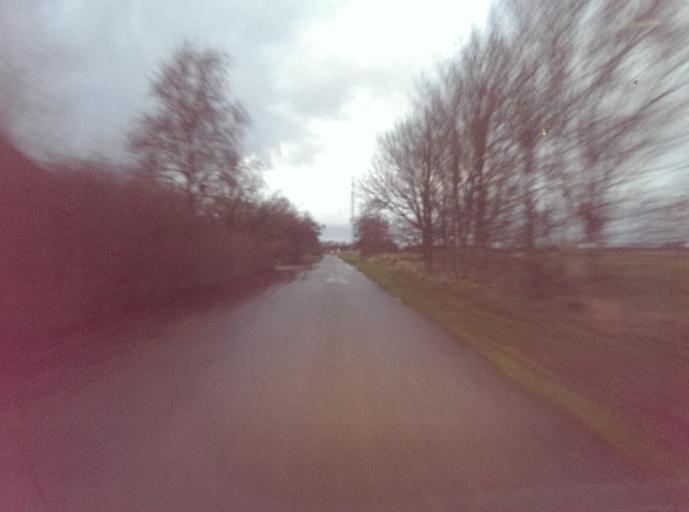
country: DK
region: South Denmark
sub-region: Esbjerg Kommune
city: Bramming
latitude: 55.4344
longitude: 8.6643
